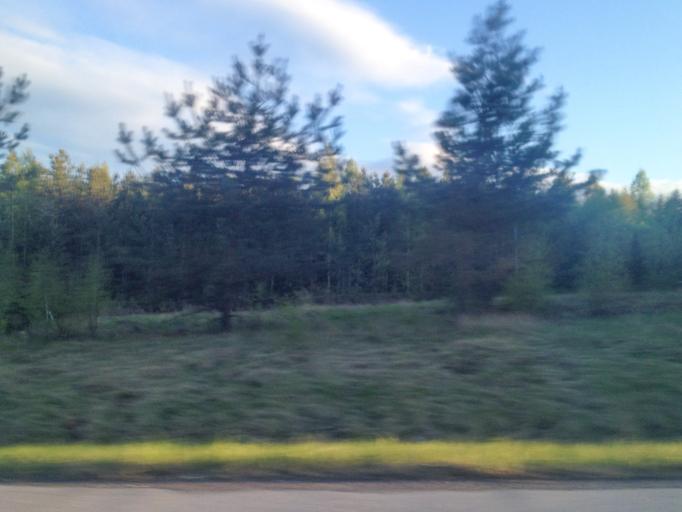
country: FI
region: Haeme
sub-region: Haemeenlinna
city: Tervakoski
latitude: 60.8529
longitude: 24.6008
